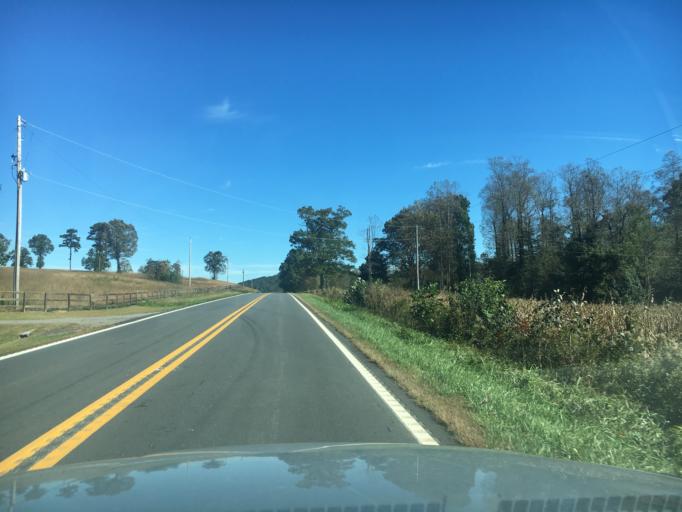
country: US
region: North Carolina
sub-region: Burke County
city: Glen Alpine
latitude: 35.5948
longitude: -81.8267
